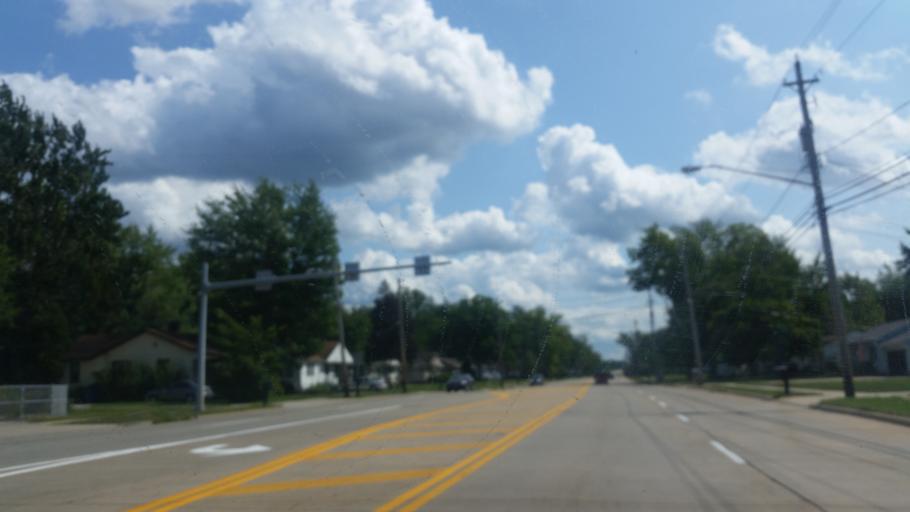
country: US
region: Ohio
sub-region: Cuyahoga County
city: North Olmsted
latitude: 41.4063
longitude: -81.9435
